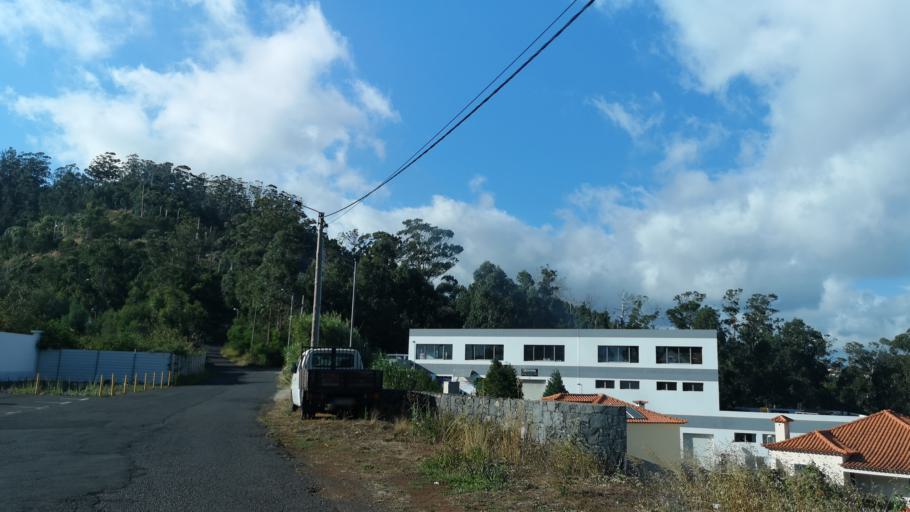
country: PT
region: Madeira
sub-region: Santa Cruz
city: Camacha
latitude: 32.6626
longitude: -16.8366
